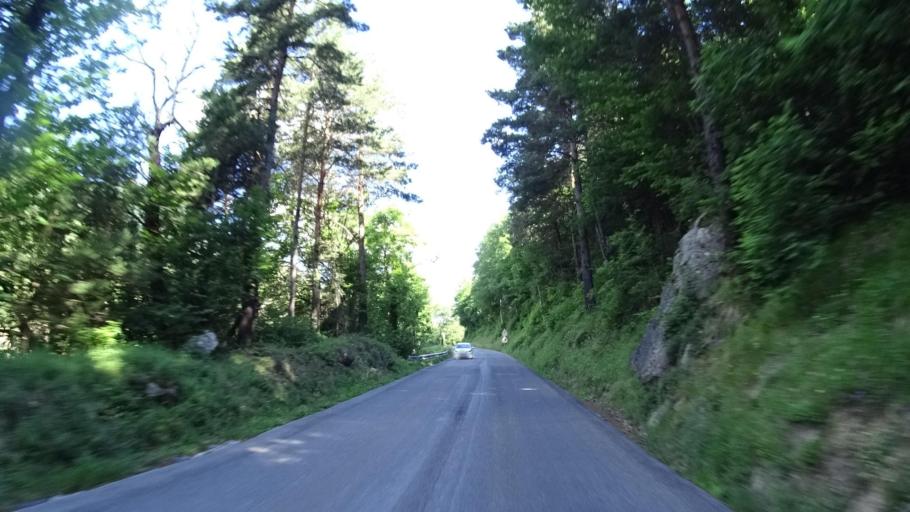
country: FR
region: Provence-Alpes-Cote d'Azur
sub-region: Departement des Alpes-de-Haute-Provence
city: Annot
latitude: 43.9759
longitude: 6.6533
